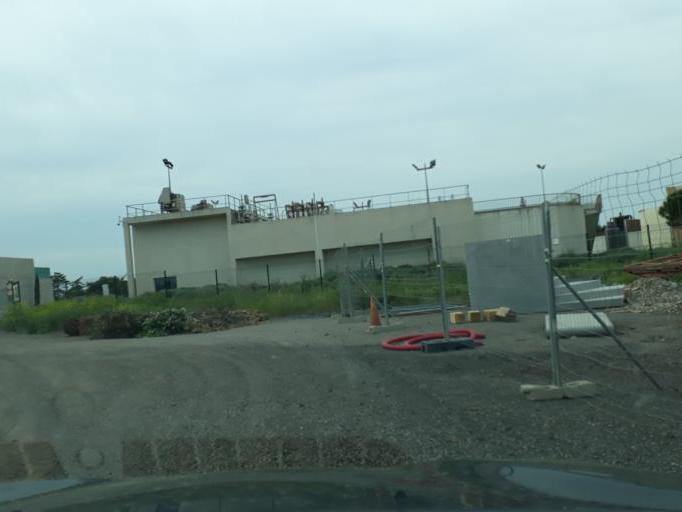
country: FR
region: Languedoc-Roussillon
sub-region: Departement de l'Herault
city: Agde
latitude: 43.2955
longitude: 3.4668
